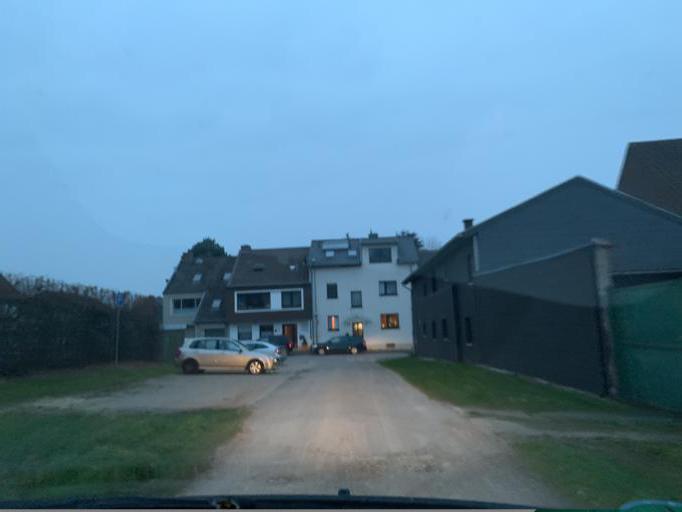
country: DE
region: North Rhine-Westphalia
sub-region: Regierungsbezirk Koln
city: Dueren
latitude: 50.7917
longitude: 6.4397
